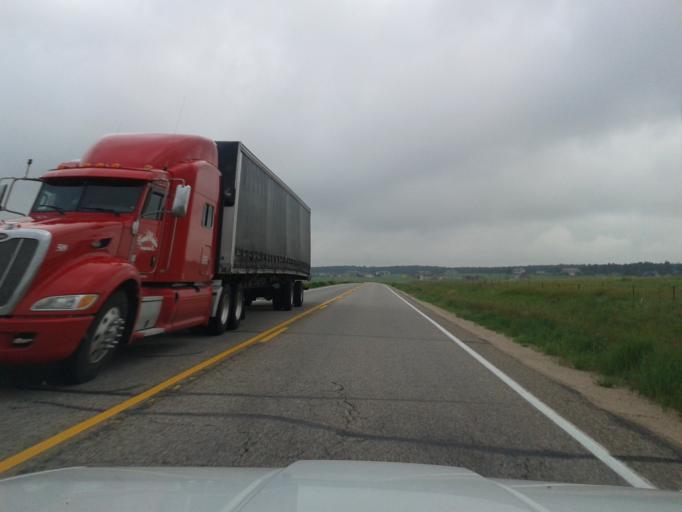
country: US
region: Colorado
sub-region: El Paso County
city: Woodmoor
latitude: 39.1171
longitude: -104.7689
